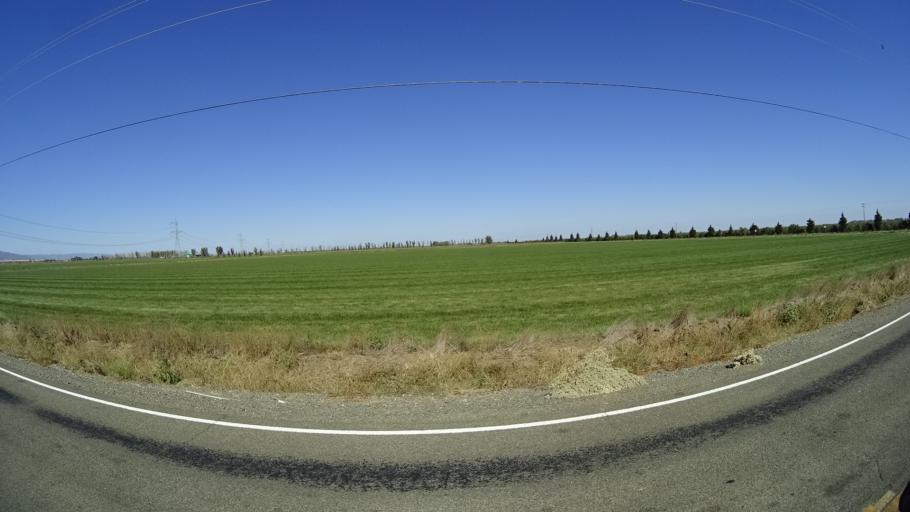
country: US
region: California
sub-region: Yolo County
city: Winters
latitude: 38.5618
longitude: -121.9068
